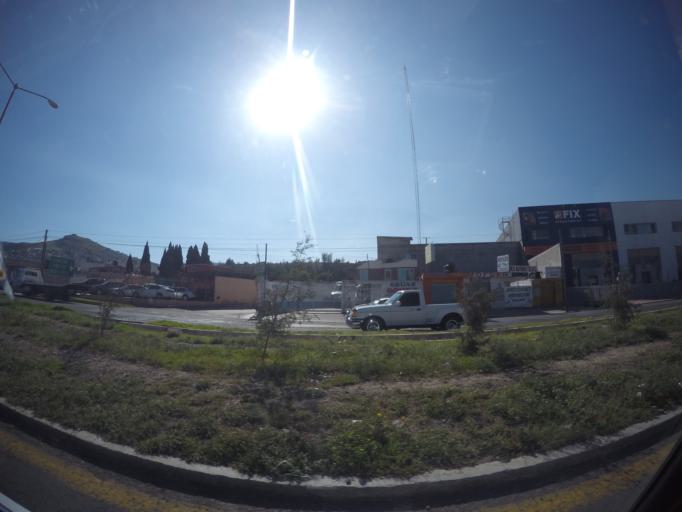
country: MX
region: Hidalgo
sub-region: Mineral de la Reforma
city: Santiago Jaltepec
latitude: 20.1086
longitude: -98.7169
